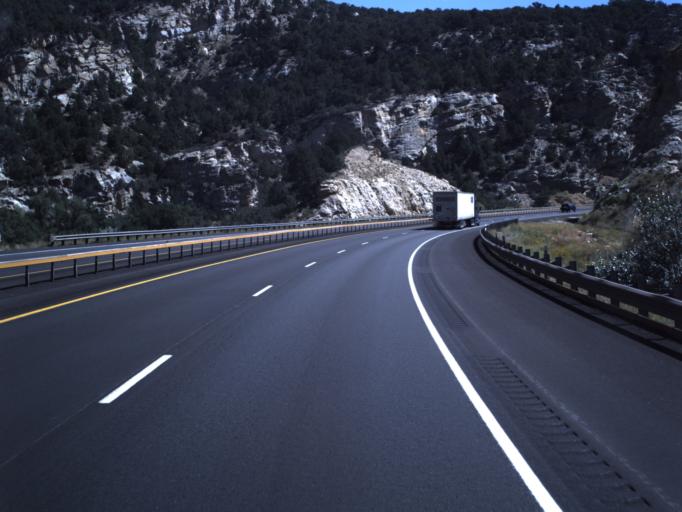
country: US
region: Utah
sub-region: Sevier County
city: Salina
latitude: 38.9052
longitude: -111.6406
